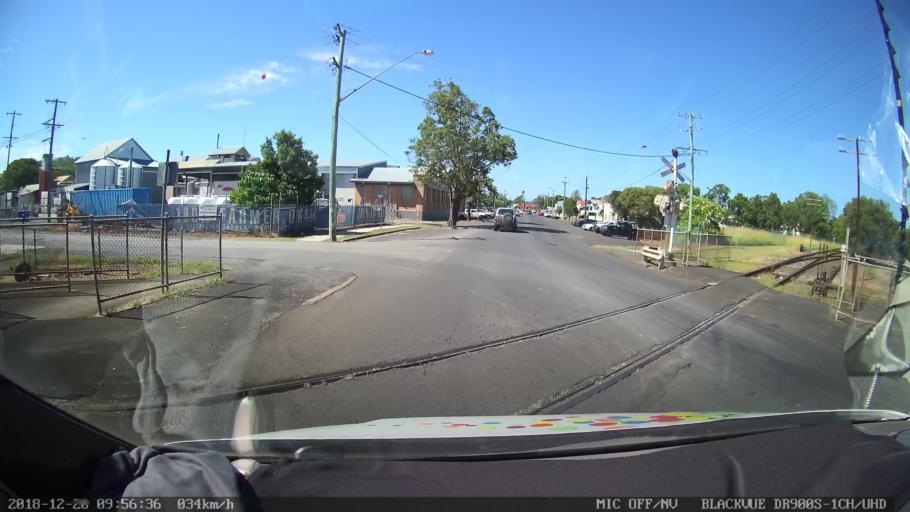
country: AU
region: New South Wales
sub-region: Lismore Municipality
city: Lismore
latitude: -28.8106
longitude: 153.2682
